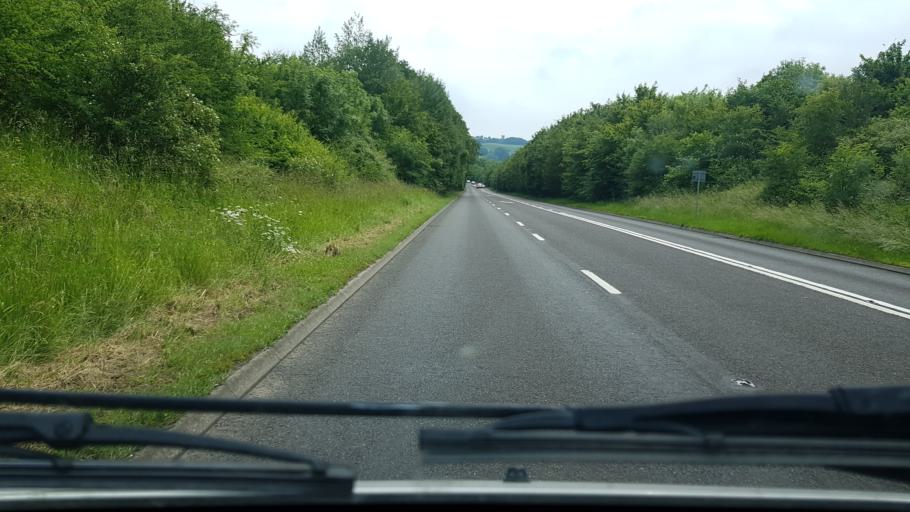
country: GB
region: England
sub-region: Worcestershire
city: Broadway
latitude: 52.0426
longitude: -1.8507
